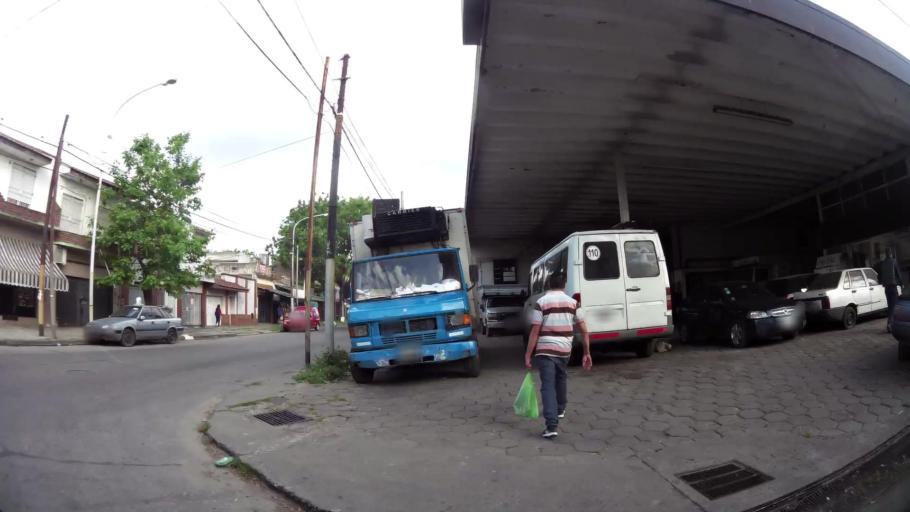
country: AR
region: Buenos Aires
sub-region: Partido de Avellaneda
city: Avellaneda
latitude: -34.6918
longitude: -58.3647
